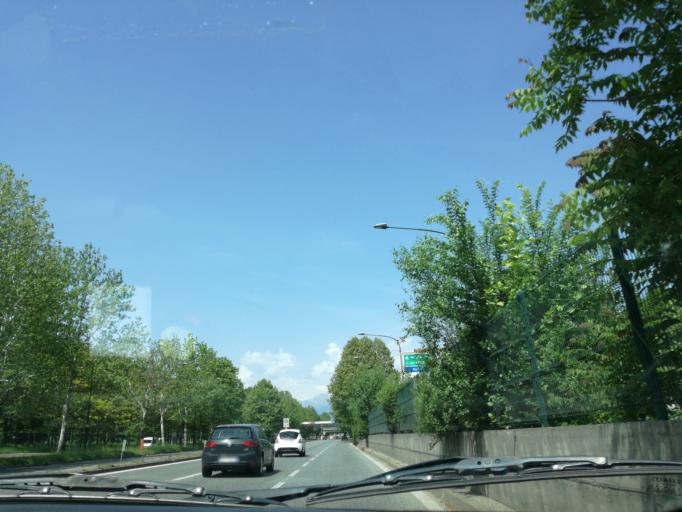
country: IT
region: Piedmont
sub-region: Provincia di Torino
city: Savonera
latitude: 45.0918
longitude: 7.6383
